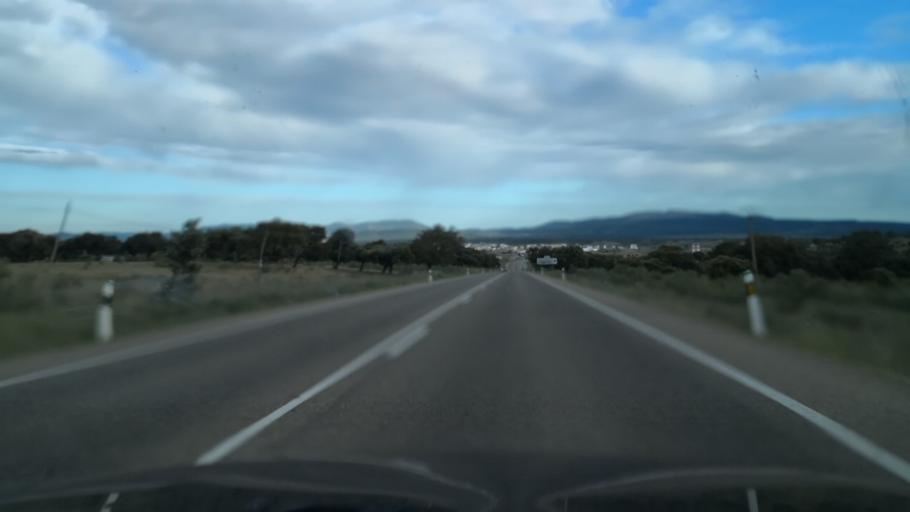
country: ES
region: Extremadura
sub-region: Provincia de Caceres
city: Torrejoncillo
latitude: 39.9126
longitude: -6.4837
